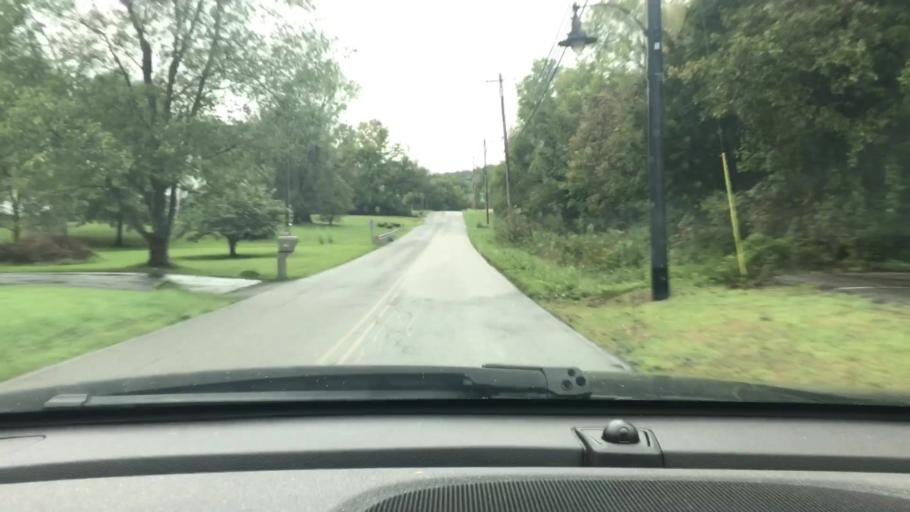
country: US
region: Tennessee
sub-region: Cheatham County
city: Kingston Springs
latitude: 36.1017
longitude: -87.1157
